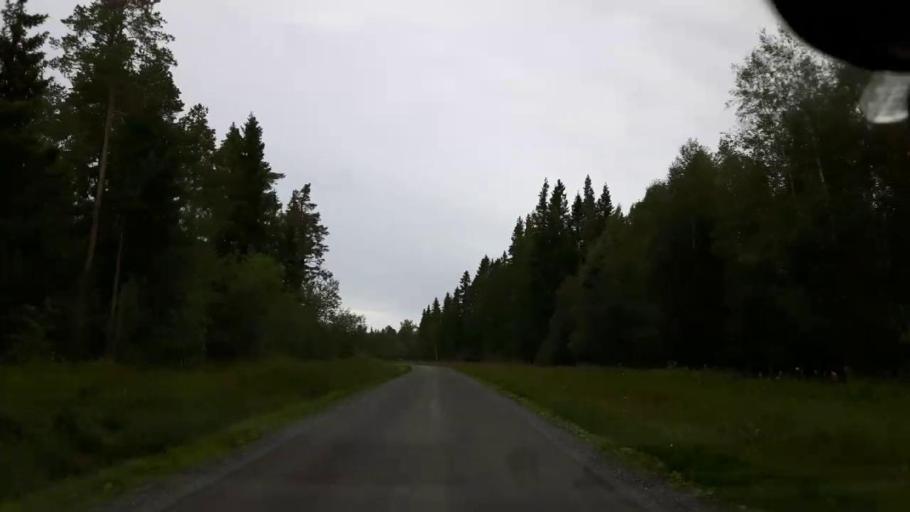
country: SE
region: Jaemtland
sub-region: Krokoms Kommun
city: Krokom
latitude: 63.2859
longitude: 14.3844
